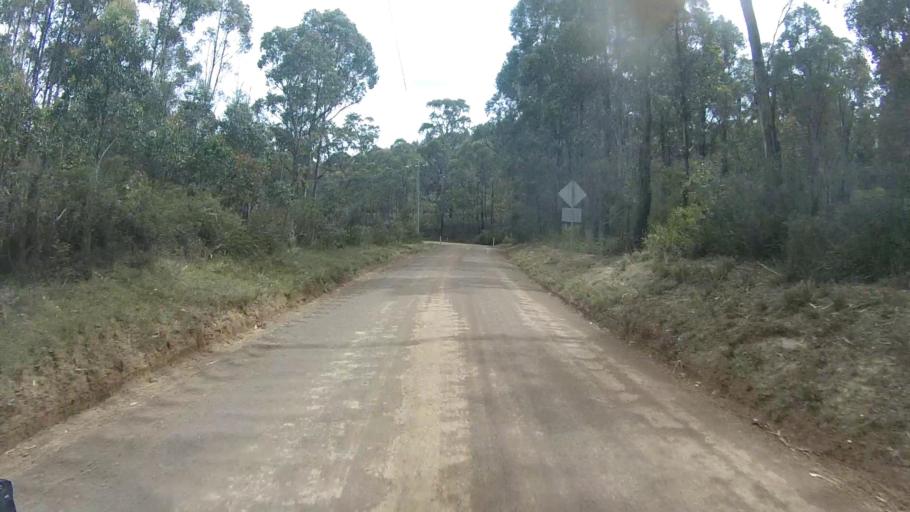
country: AU
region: Tasmania
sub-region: Sorell
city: Sorell
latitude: -42.7670
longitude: 147.8054
